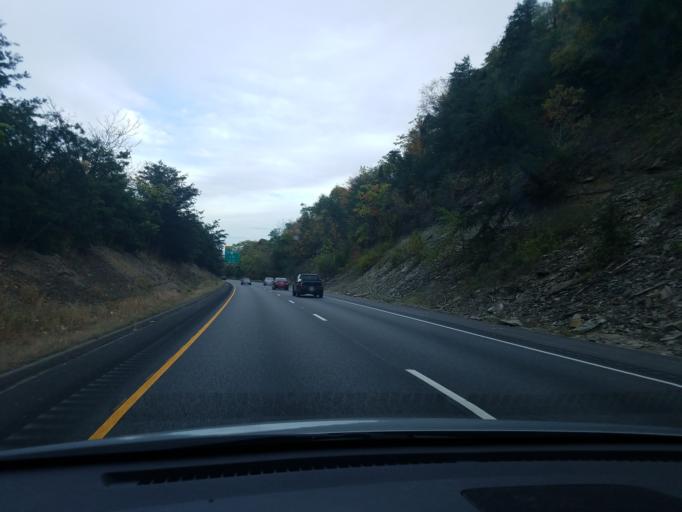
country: US
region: Indiana
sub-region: Floyd County
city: New Albany
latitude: 38.3013
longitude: -85.8697
